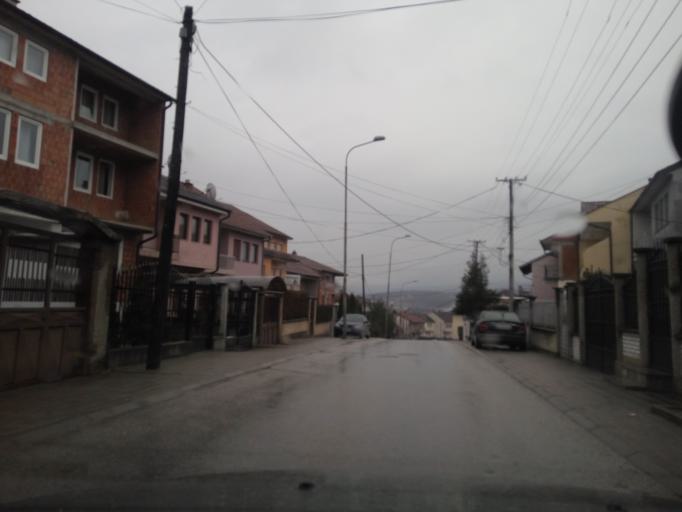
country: XK
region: Gjakova
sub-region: Komuna e Gjakoves
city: Gjakove
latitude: 42.3675
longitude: 20.4422
